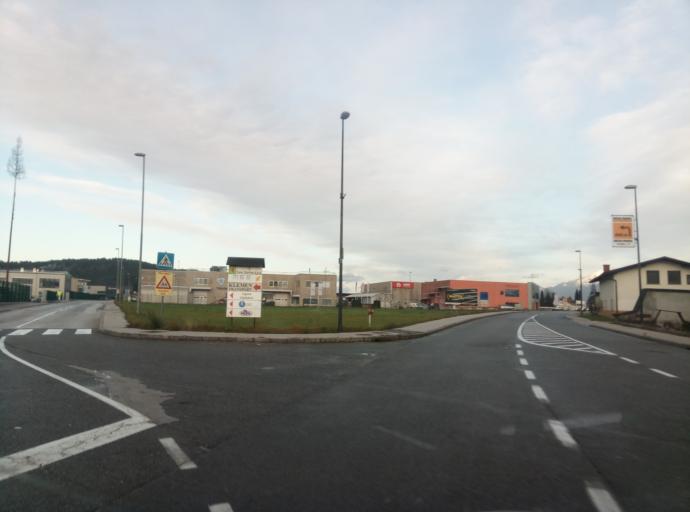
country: SI
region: Menges
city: Menges
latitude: 46.1738
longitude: 14.5688
